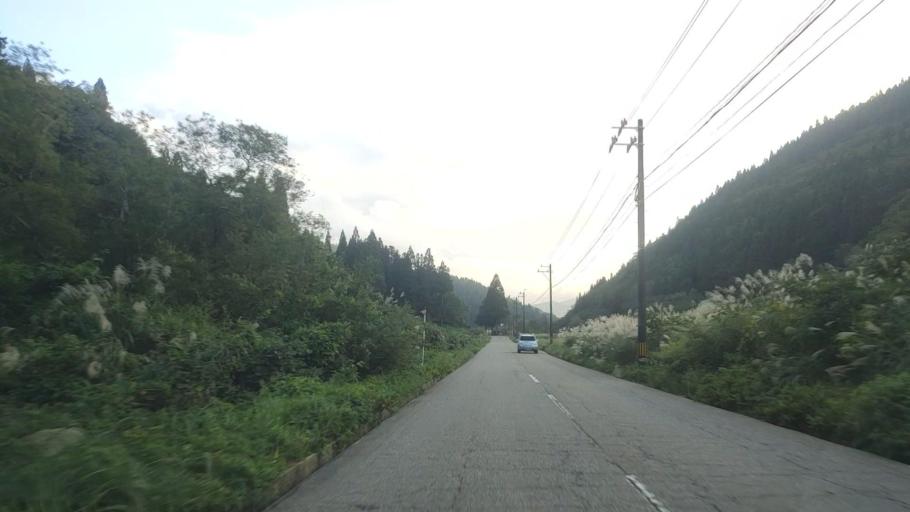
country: JP
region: Toyama
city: Yatsuomachi-higashikumisaka
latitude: 36.4726
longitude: 137.0492
